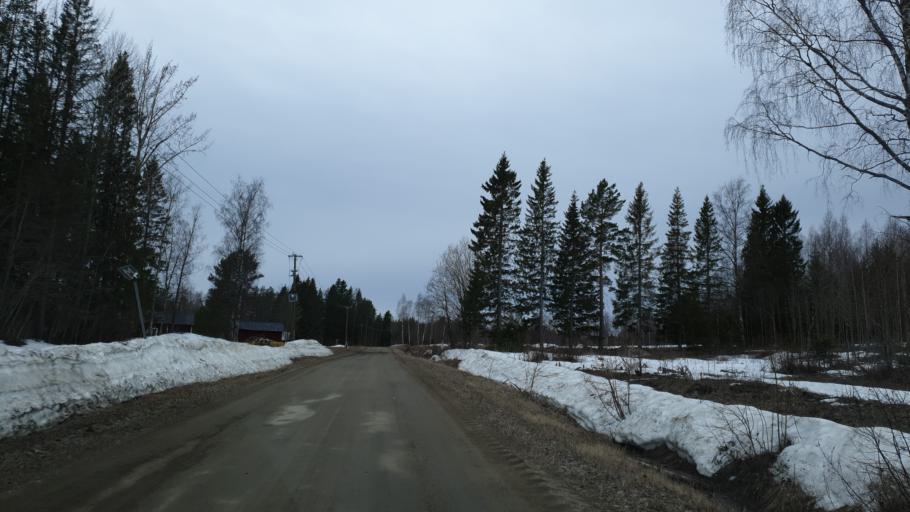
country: SE
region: Vaesterbotten
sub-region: Robertsfors Kommun
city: Robertsfors
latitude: 64.3905
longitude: 20.9707
